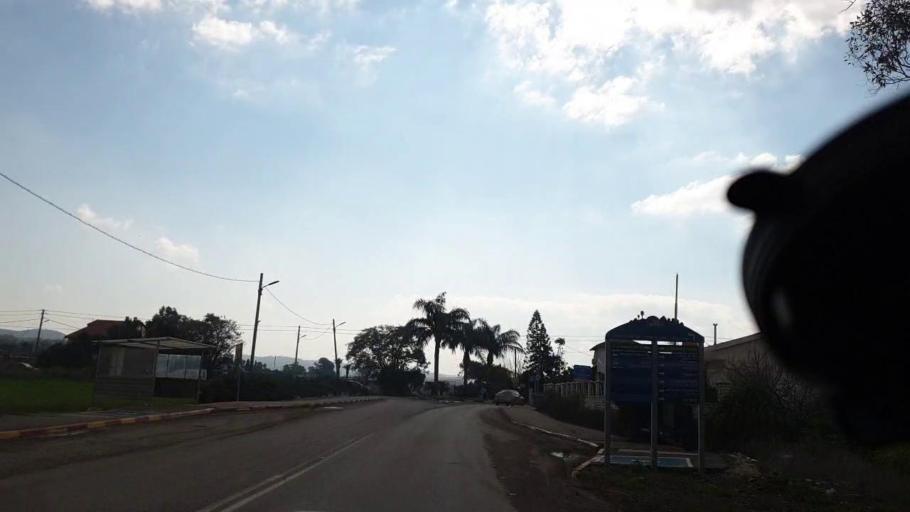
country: IL
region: Haifa
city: Rekhasim
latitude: 32.7508
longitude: 35.0876
